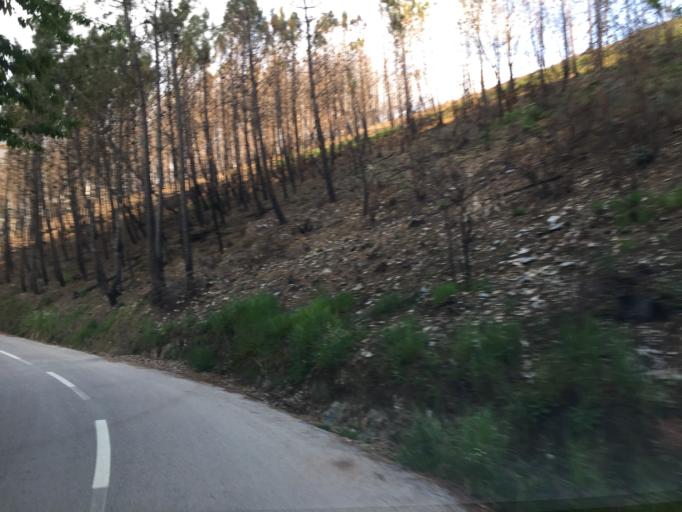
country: PT
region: Coimbra
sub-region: Arganil
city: Arganil
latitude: 40.1347
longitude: -7.9993
